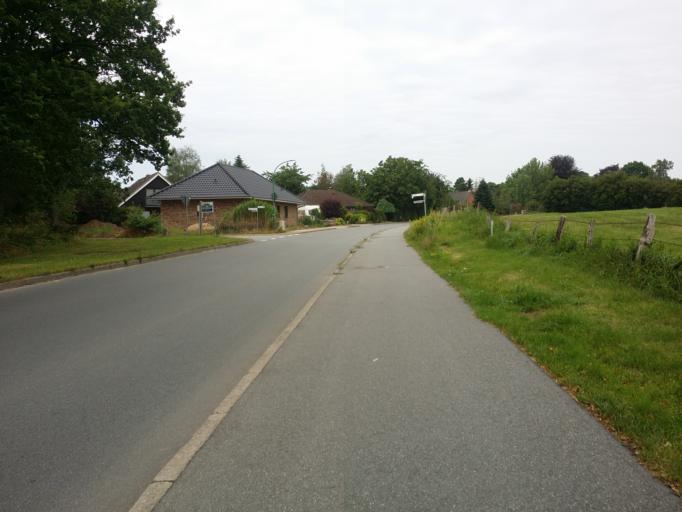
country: DE
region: Schleswig-Holstein
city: Oldendorf
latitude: 53.9456
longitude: 9.4649
